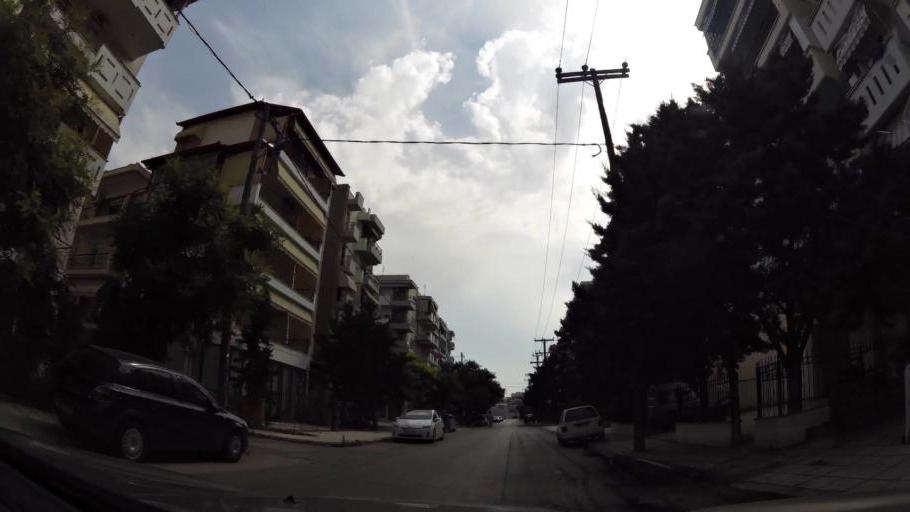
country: GR
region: Central Macedonia
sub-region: Nomos Thessalonikis
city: Stavroupoli
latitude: 40.6827
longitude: 22.9317
